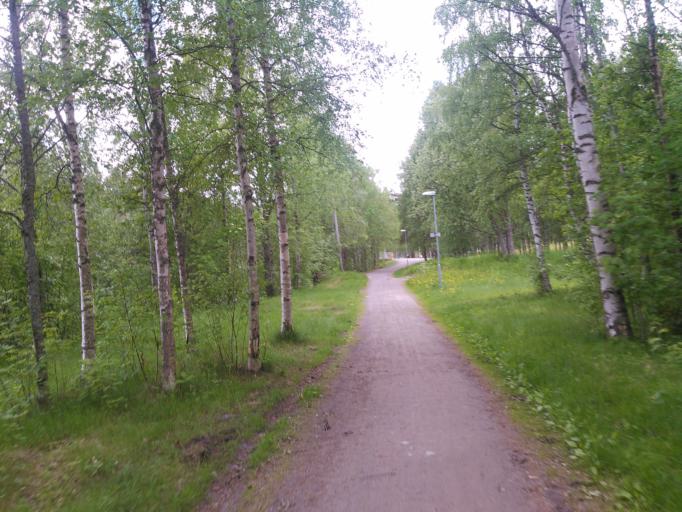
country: SE
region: Vaesterbotten
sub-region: Umea Kommun
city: Umea
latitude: 63.8253
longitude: 20.2241
